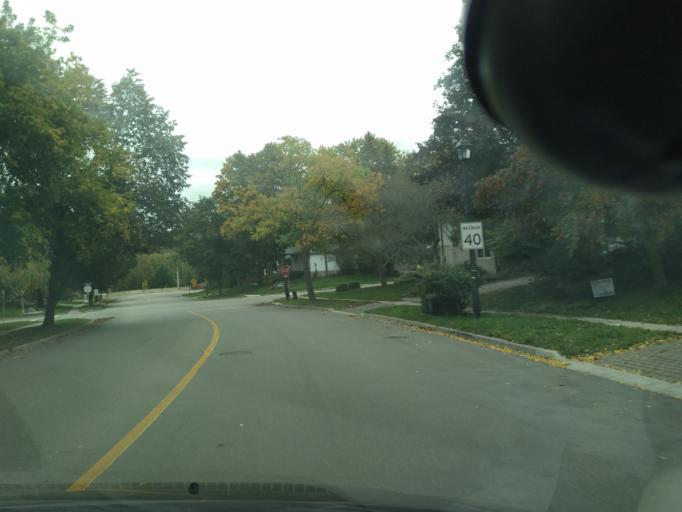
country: CA
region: Ontario
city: Newmarket
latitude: 44.0460
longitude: -79.4604
